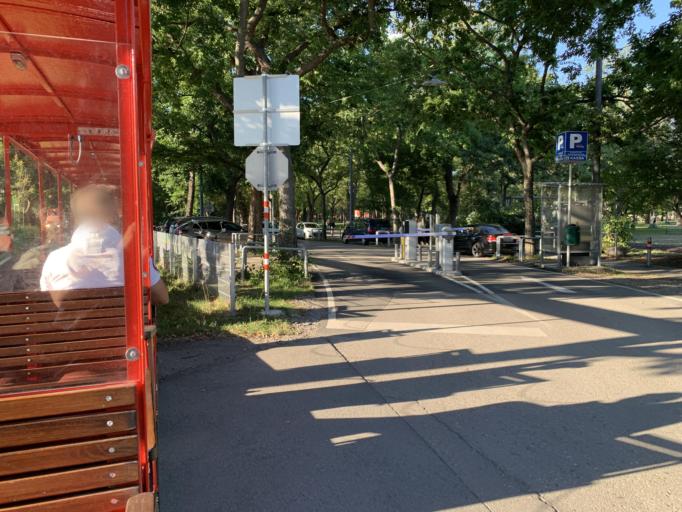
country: AT
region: Vienna
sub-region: Wien Stadt
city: Vienna
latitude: 48.2109
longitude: 16.4059
